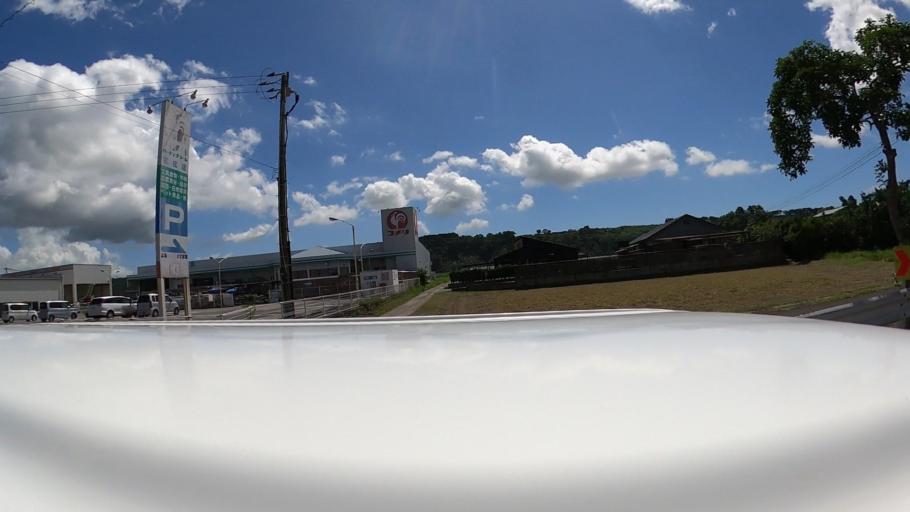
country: JP
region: Miyazaki
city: Tsuma
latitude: 32.0970
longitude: 131.4090
